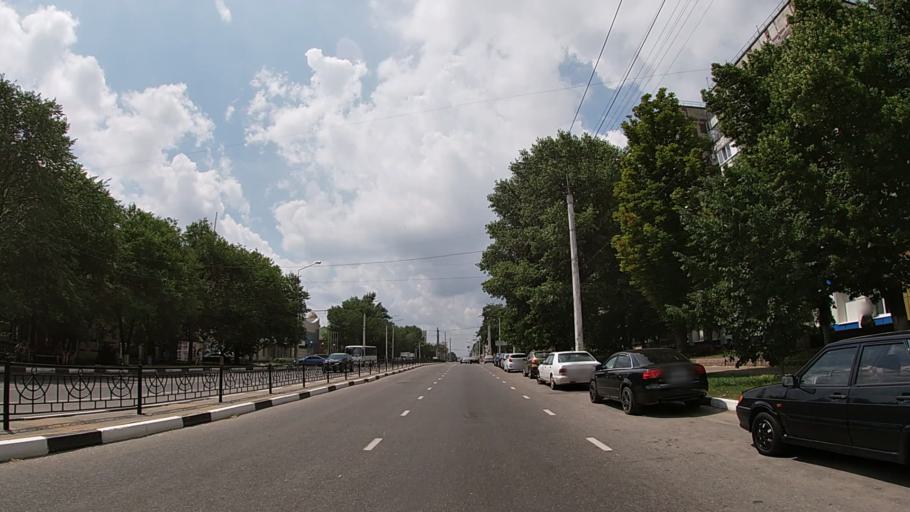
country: RU
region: Belgorod
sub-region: Belgorodskiy Rayon
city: Belgorod
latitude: 50.6131
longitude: 36.5900
